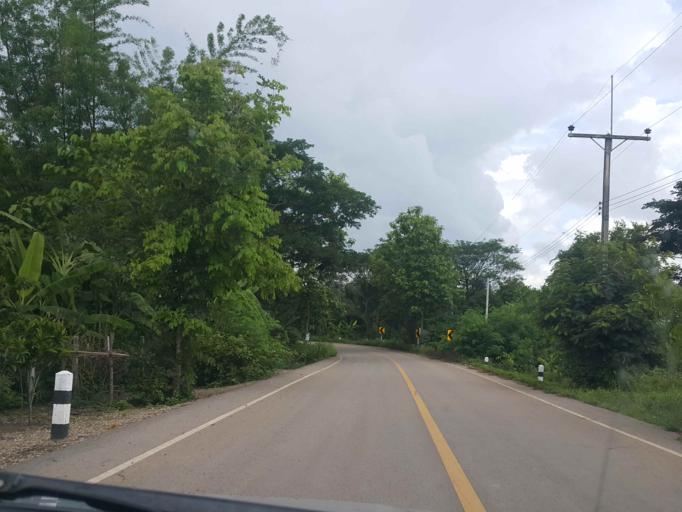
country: TH
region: Phayao
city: Dok Kham Tai
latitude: 19.0400
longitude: 99.9549
